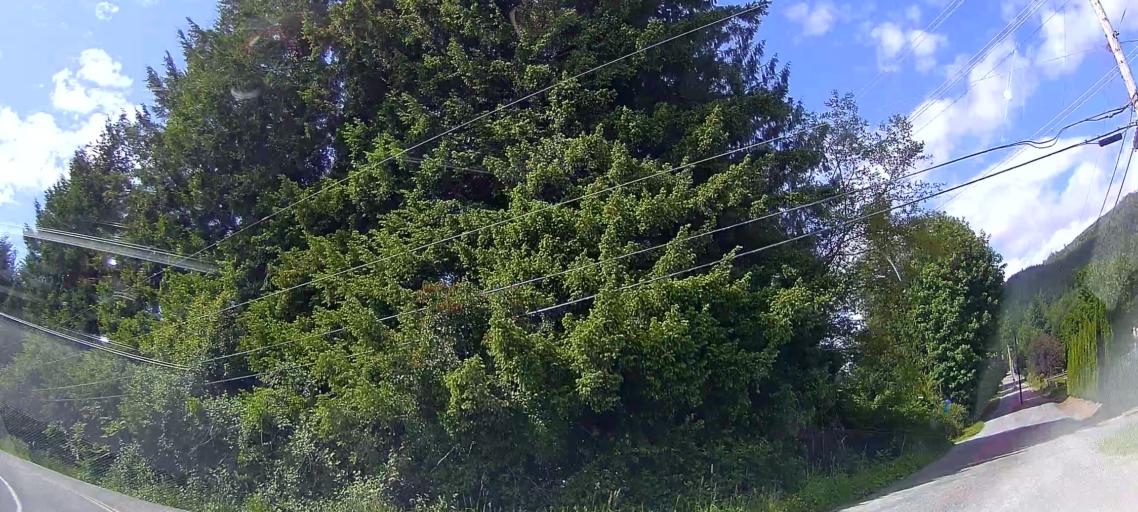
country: US
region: Washington
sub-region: Skagit County
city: Sedro-Woolley
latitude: 48.5649
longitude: -122.2109
